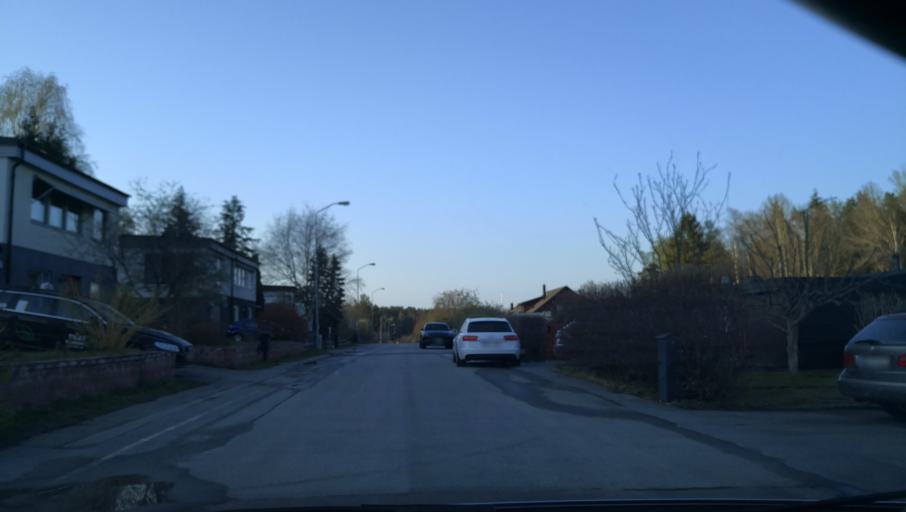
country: SE
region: Stockholm
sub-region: Varmdo Kommun
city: Hemmesta
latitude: 59.3180
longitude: 18.5037
